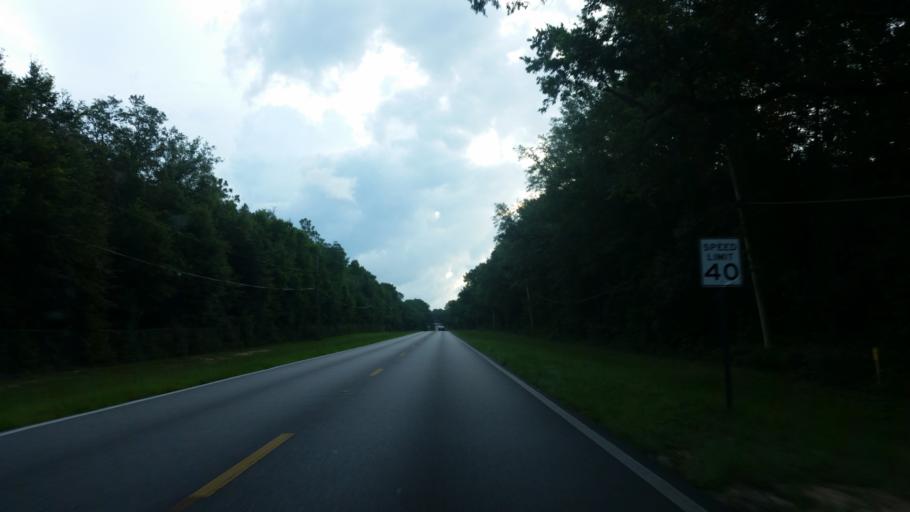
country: US
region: Florida
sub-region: Escambia County
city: Bellview
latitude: 30.4491
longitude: -87.3017
